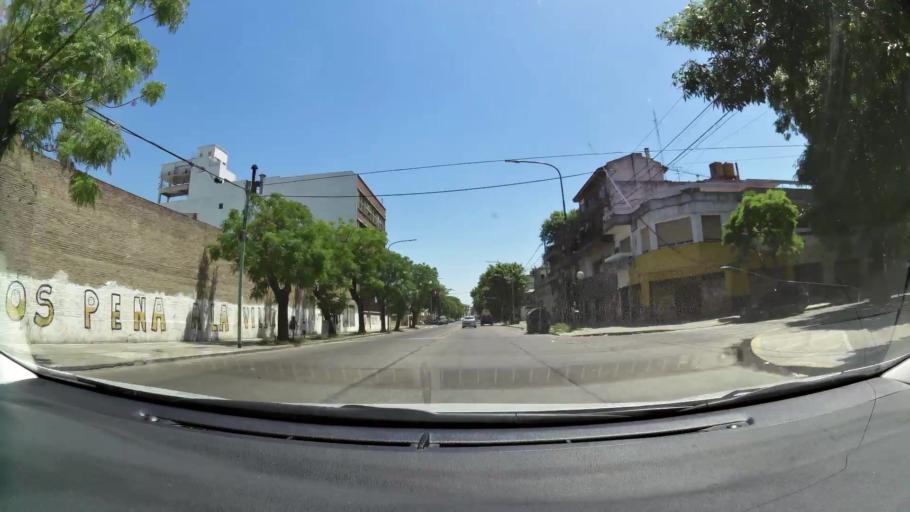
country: AR
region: Buenos Aires
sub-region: Partido de Avellaneda
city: Avellaneda
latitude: -34.6513
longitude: -58.3914
